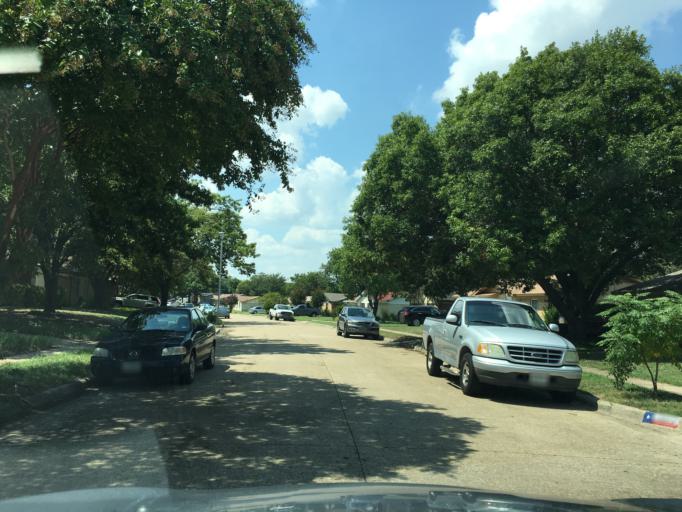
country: US
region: Texas
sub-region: Dallas County
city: Garland
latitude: 32.9427
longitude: -96.6508
